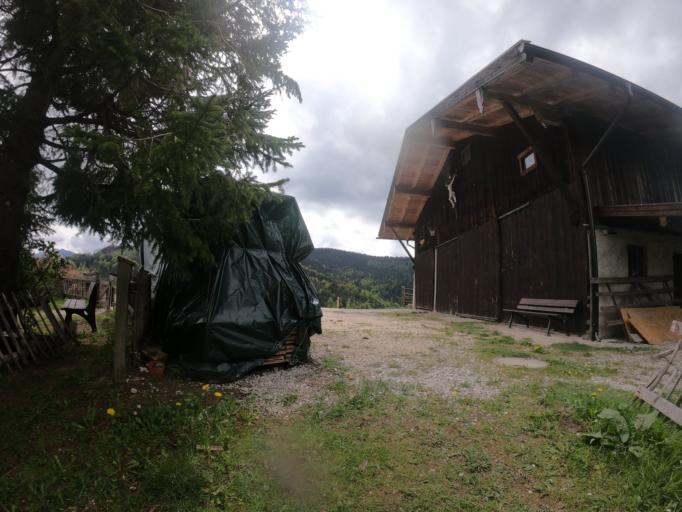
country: DE
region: Bavaria
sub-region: Upper Bavaria
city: Bergen
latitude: 47.7922
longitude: 12.6149
